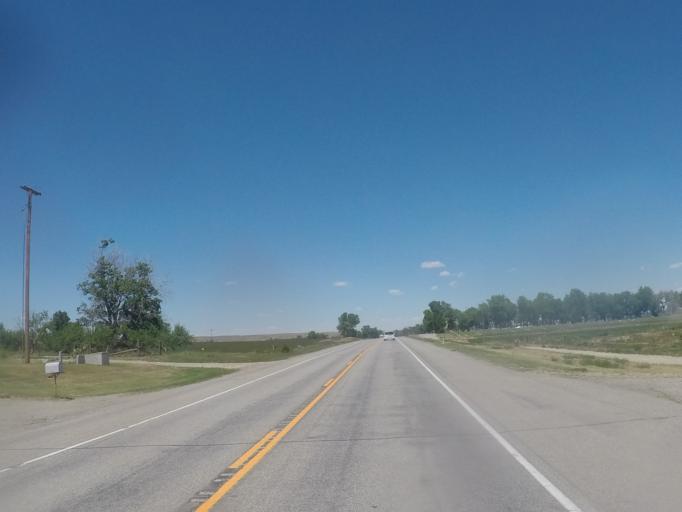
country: US
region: Montana
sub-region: Yellowstone County
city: Laurel
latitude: 45.4852
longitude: -108.8631
